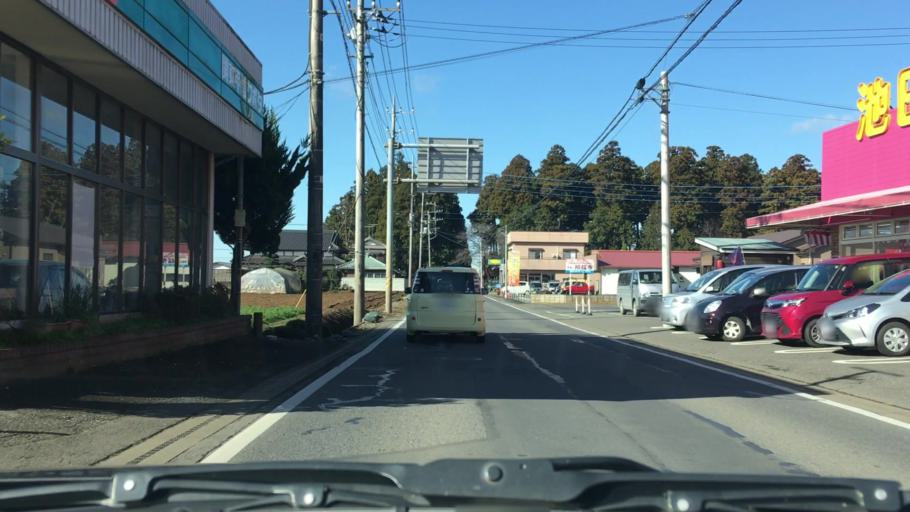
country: JP
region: Chiba
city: Sawara
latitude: 35.7971
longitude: 140.4521
